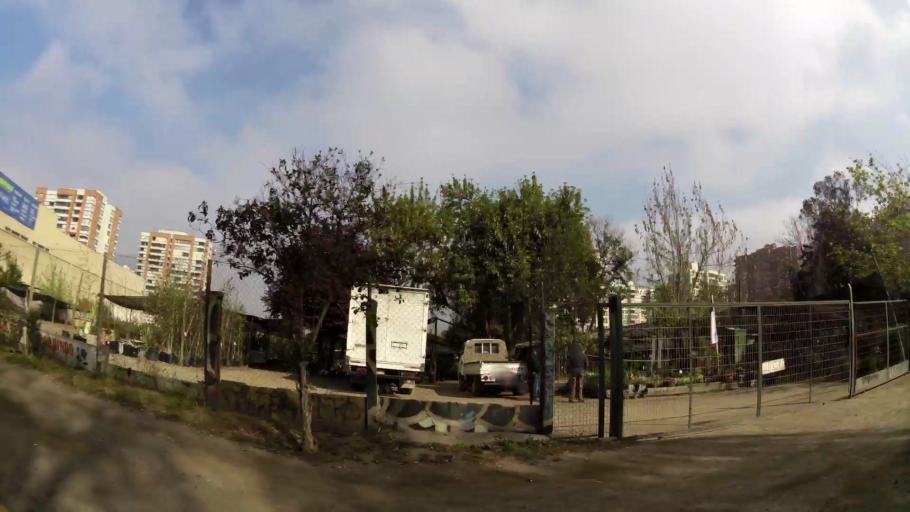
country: CL
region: Santiago Metropolitan
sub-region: Provincia de Santiago
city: Villa Presidente Frei, Nunoa, Santiago, Chile
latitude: -33.4225
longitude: -70.5378
